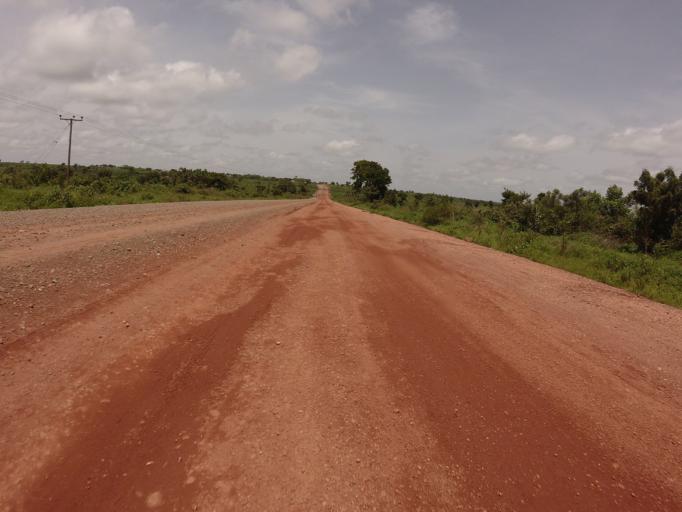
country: GH
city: Kpandae
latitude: 8.6286
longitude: 0.2251
